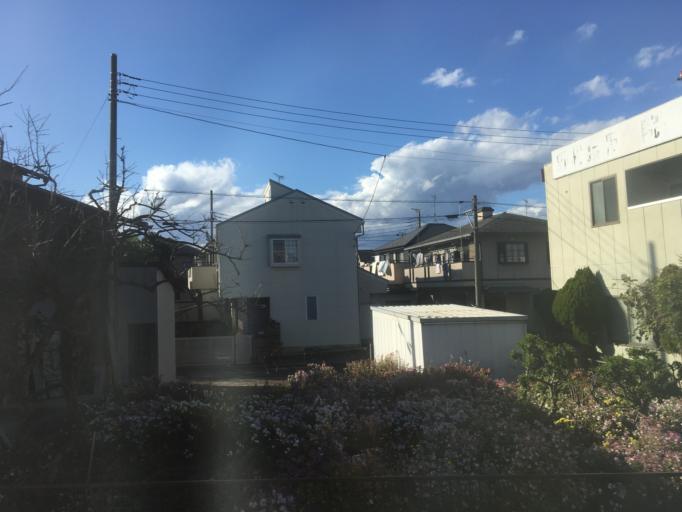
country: JP
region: Saitama
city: Sakado
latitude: 35.9621
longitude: 139.3892
